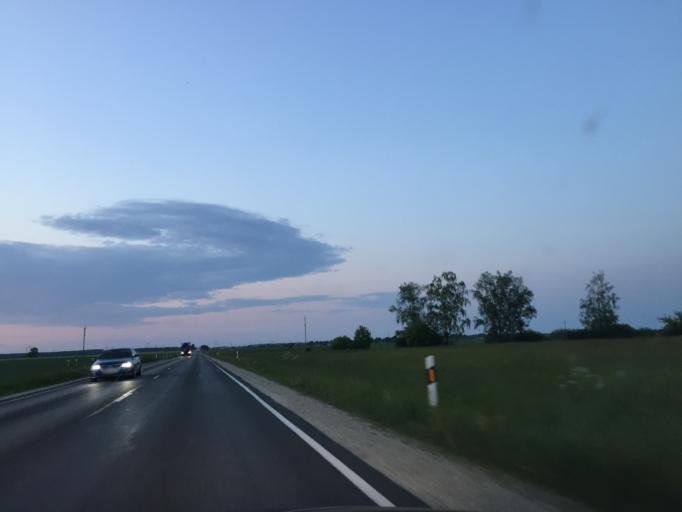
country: LT
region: Siauliu apskritis
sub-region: Joniskis
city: Joniskis
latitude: 56.0937
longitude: 23.4730
